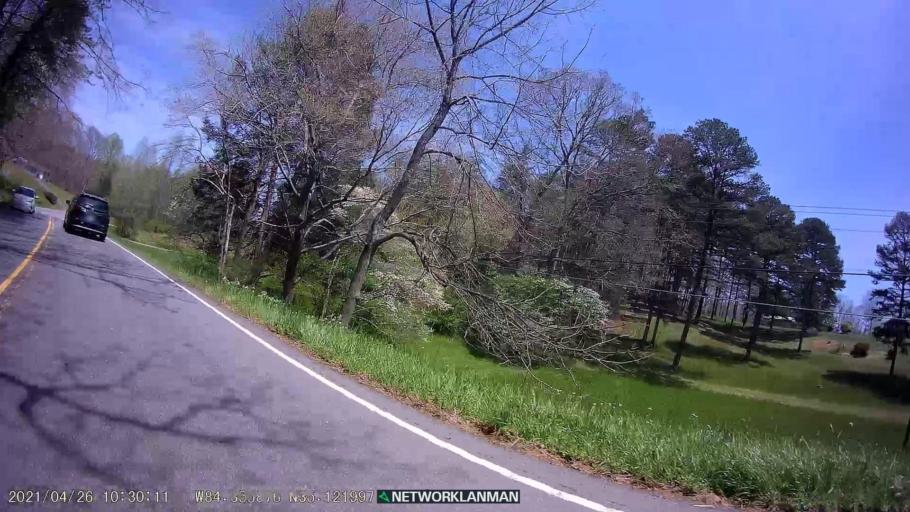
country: US
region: Georgia
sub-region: Fannin County
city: McCaysville
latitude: 35.1222
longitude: -84.3558
